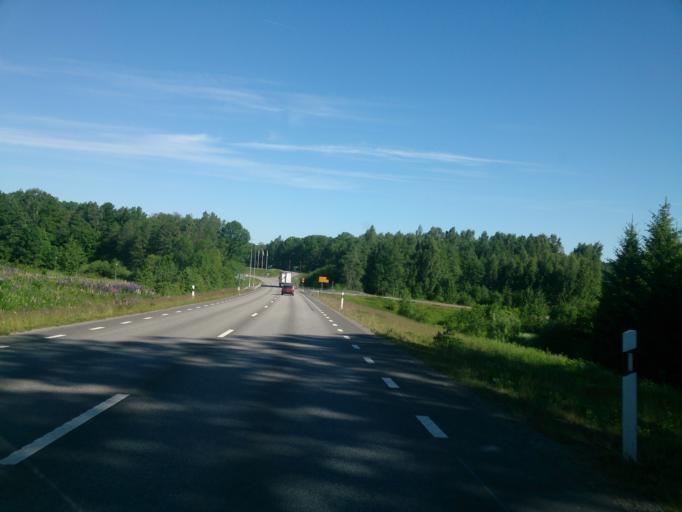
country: SE
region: OEstergoetland
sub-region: Atvidabergs Kommun
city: Atvidaberg
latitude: 58.1922
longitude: 16.0221
